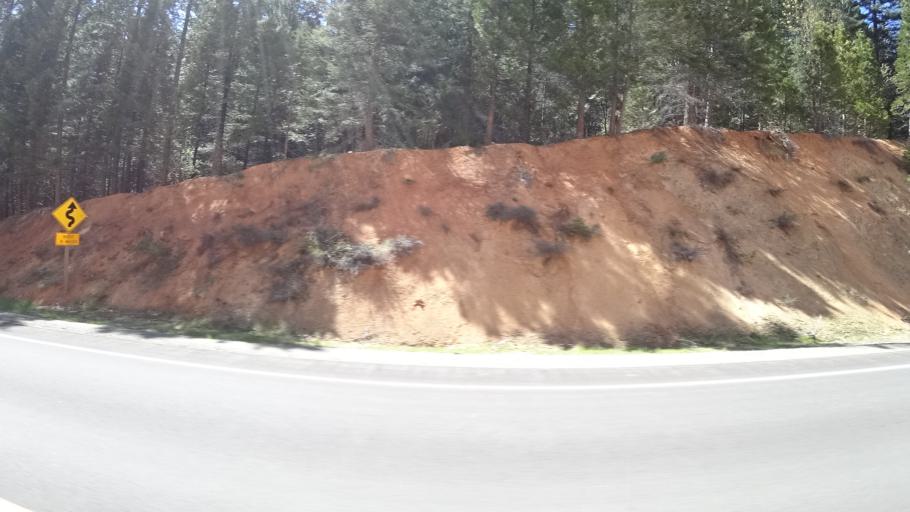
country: US
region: California
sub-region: Trinity County
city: Lewiston
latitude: 40.8949
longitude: -122.7922
